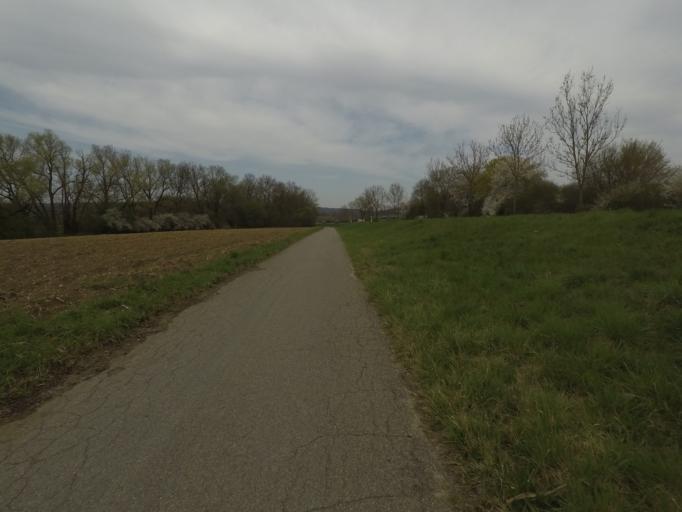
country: DE
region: Baden-Wuerttemberg
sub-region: Tuebingen Region
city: Gomaringen
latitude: 48.4576
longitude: 9.0776
